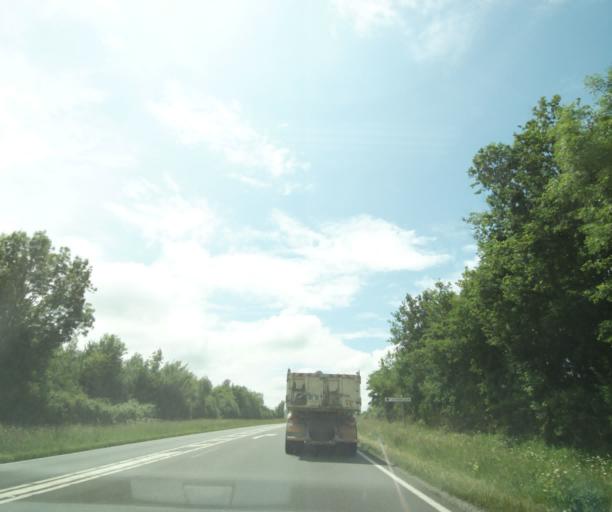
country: FR
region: Poitou-Charentes
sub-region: Departement des Deux-Sevres
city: Champdeniers-Saint-Denis
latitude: 46.4757
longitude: -0.3617
